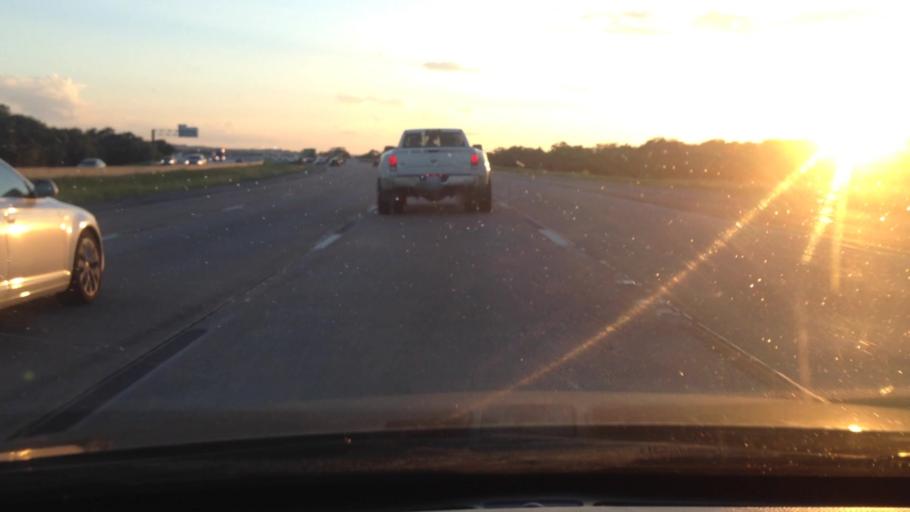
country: US
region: Texas
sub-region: Tarrant County
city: Lake Worth
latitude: 32.7969
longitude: -97.4483
